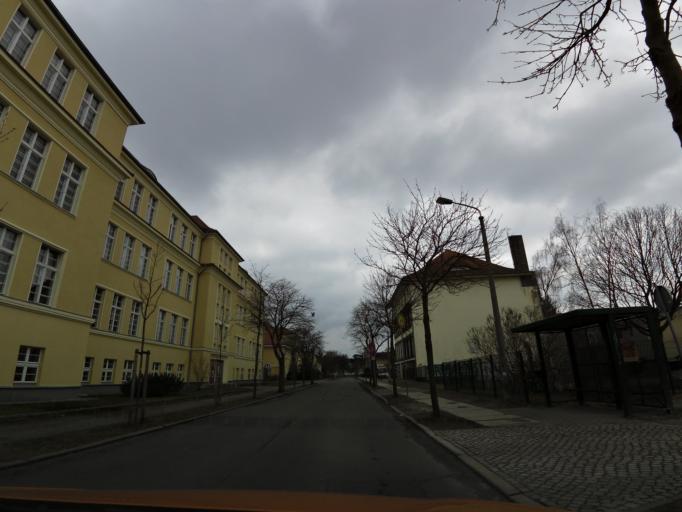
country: DE
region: Brandenburg
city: Rathenow
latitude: 52.6107
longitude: 12.3492
